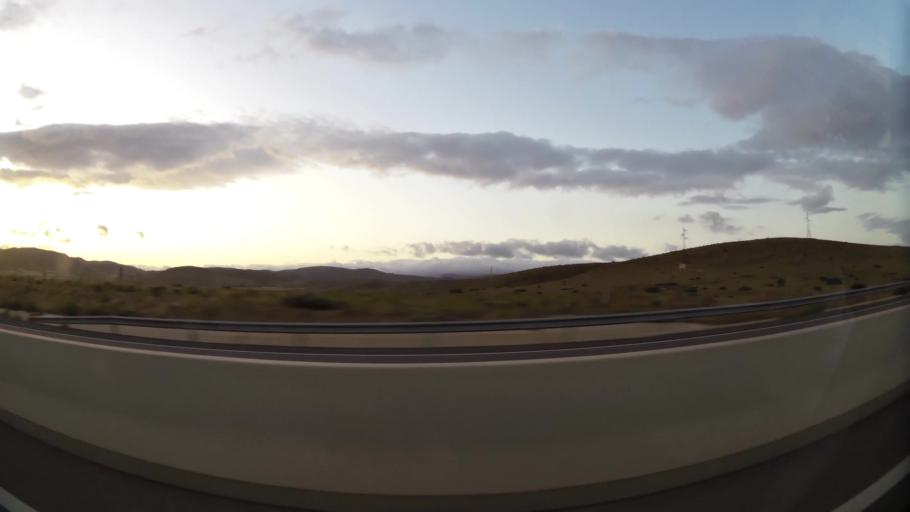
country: MA
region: Oriental
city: El Aioun
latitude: 34.6058
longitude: -2.5945
